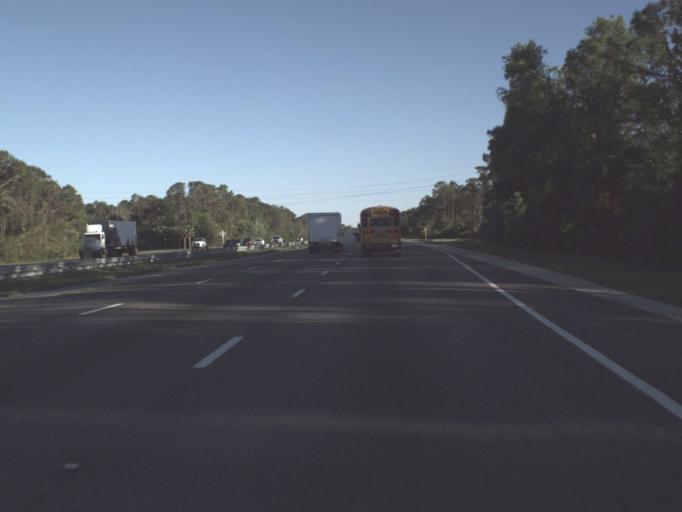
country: US
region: Florida
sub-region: Flagler County
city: Flagler Beach
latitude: 29.4103
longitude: -81.1582
